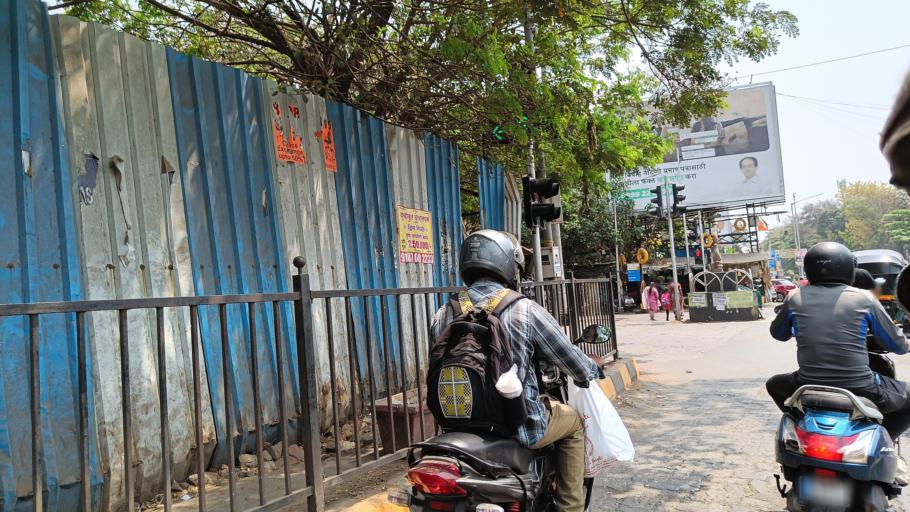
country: IN
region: Maharashtra
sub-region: Mumbai Suburban
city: Mumbai
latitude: 19.0850
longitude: 72.8319
